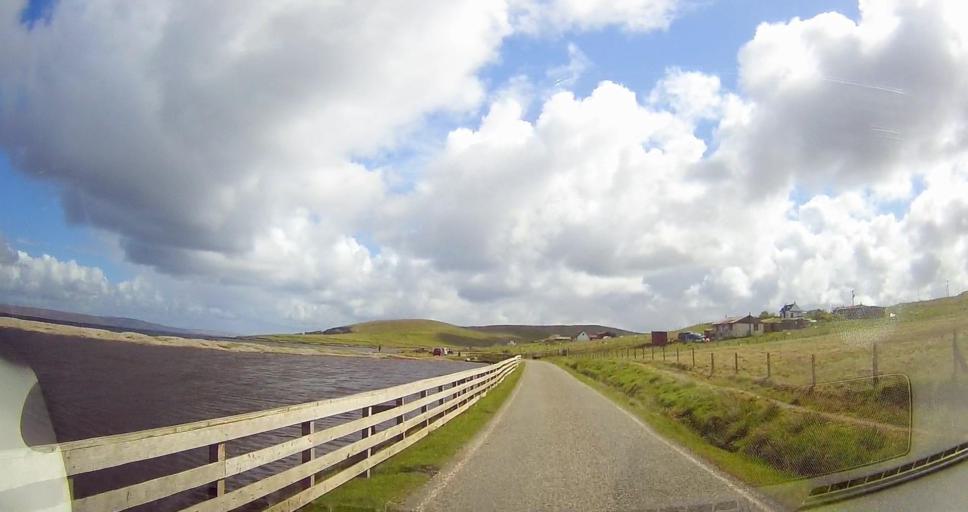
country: GB
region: Scotland
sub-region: Shetland Islands
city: Lerwick
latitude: 60.5833
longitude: -1.3368
